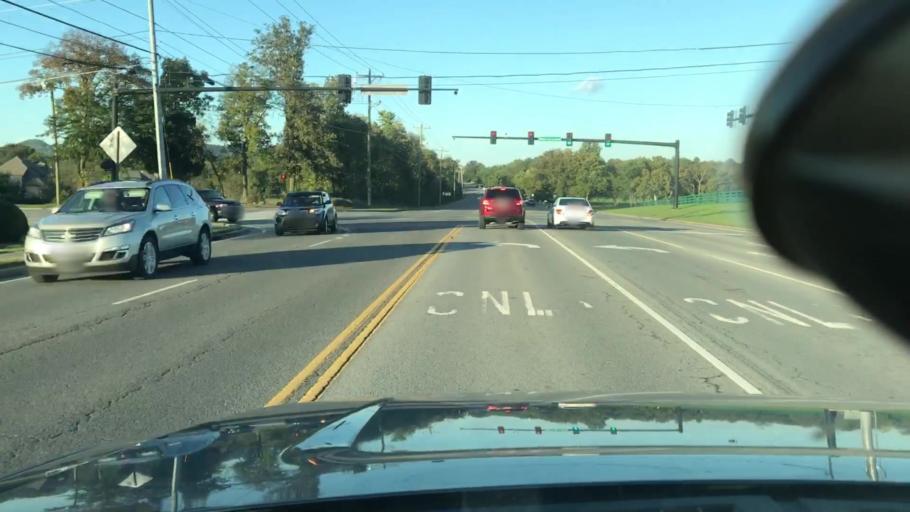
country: US
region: Tennessee
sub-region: Williamson County
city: Brentwood Estates
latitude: 36.0124
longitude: -86.8011
